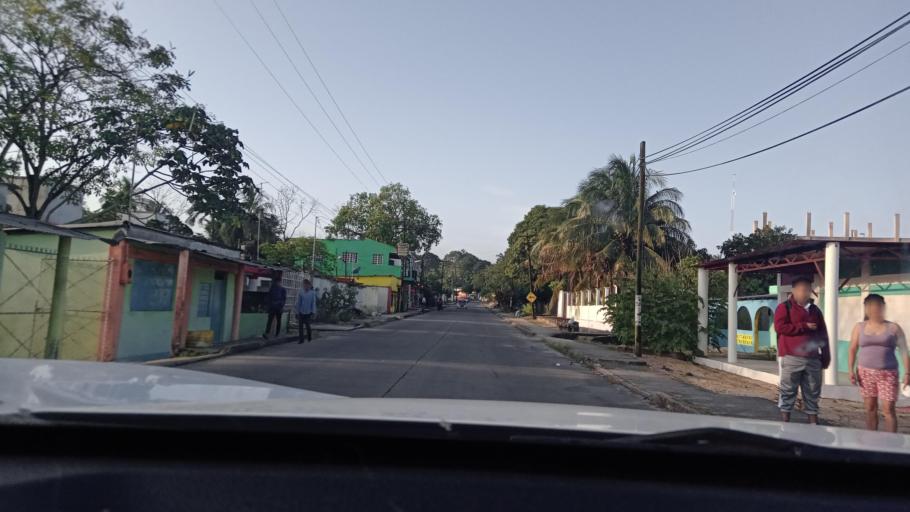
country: MX
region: Veracruz
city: Las Choapas
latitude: 17.8827
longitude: -94.0974
